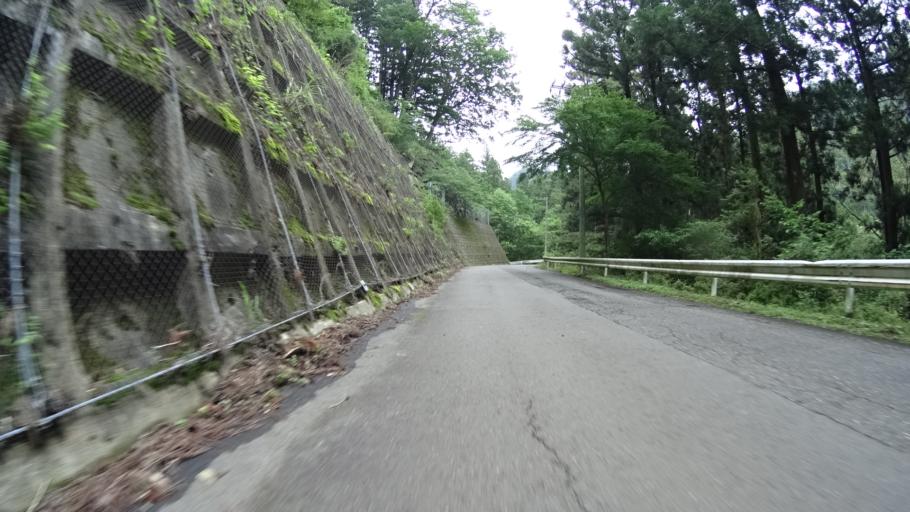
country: JP
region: Kanagawa
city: Hadano
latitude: 35.4685
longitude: 139.2168
